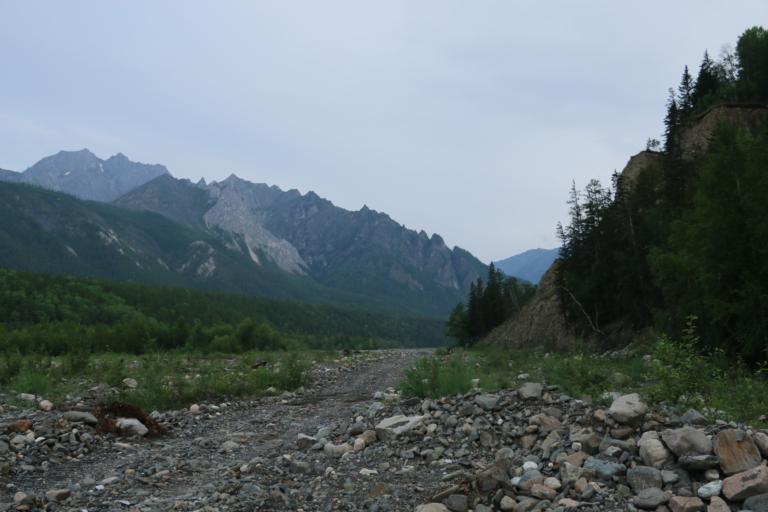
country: RU
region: Respublika Buryatiya
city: Novyy Uoyan
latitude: 56.2209
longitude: 111.5092
